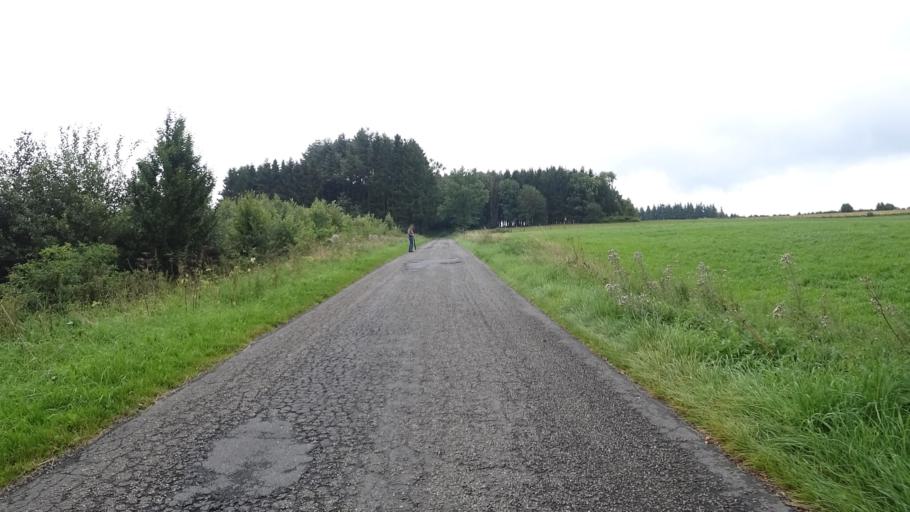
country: BE
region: Wallonia
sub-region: Province du Luxembourg
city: Chiny
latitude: 49.8096
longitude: 5.3348
